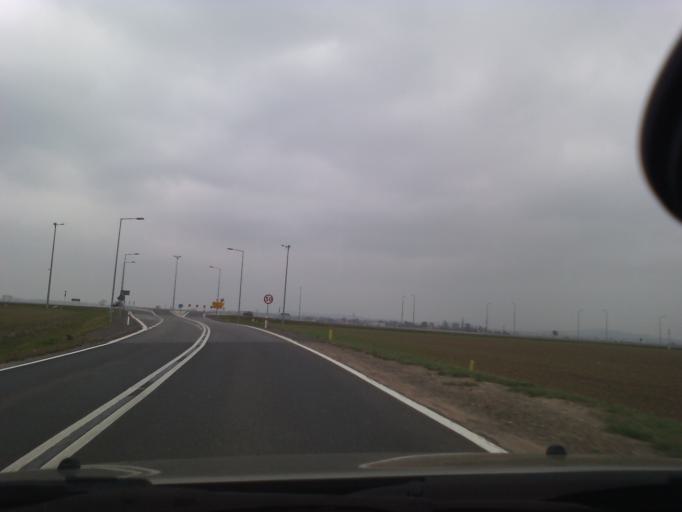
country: PL
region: Lower Silesian Voivodeship
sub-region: Powiat walbrzyski
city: Stare Bogaczowice
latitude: 50.9148
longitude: 16.2513
